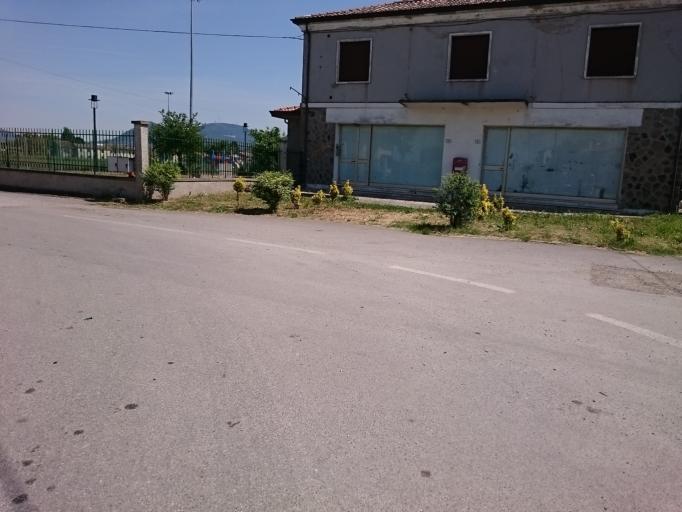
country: IT
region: Veneto
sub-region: Provincia di Padova
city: Lozzo Atestino
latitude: 45.2593
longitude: 11.6193
